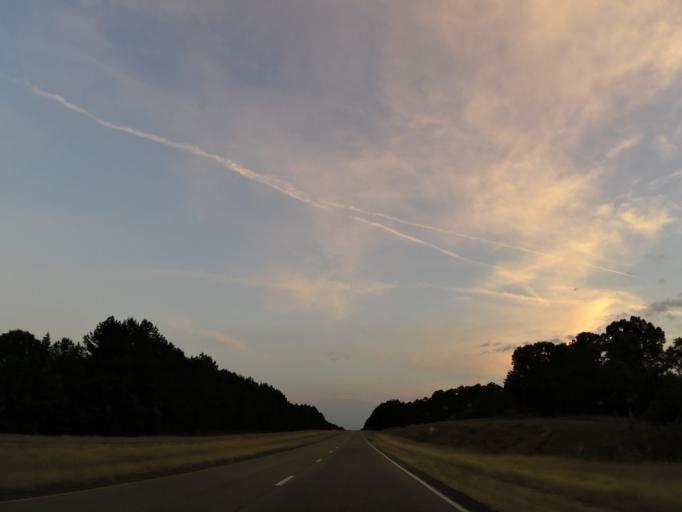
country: US
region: Mississippi
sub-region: Kemper County
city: De Kalb
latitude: 32.6822
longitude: -88.4899
